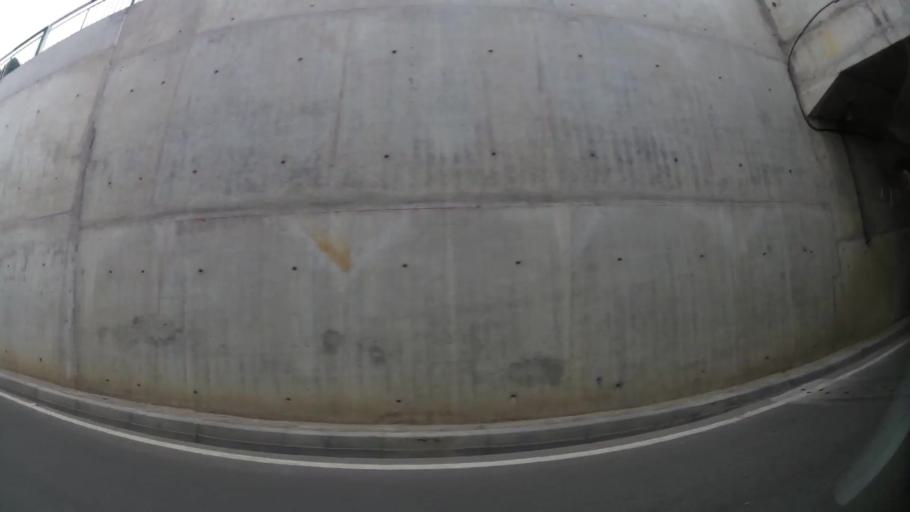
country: MA
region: Fes-Boulemane
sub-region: Fes
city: Fes
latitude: 34.0490
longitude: -5.0017
